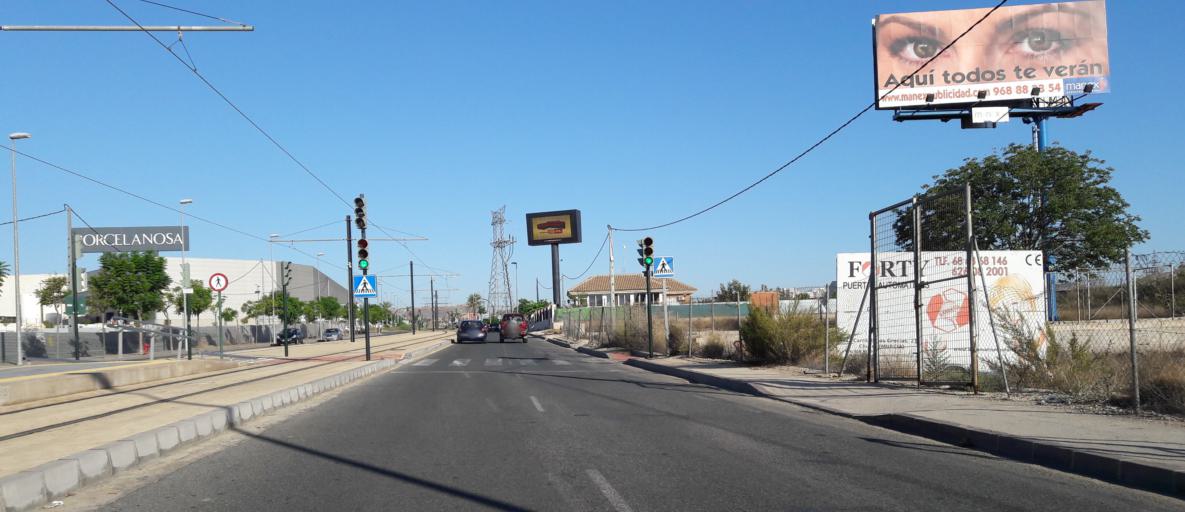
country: ES
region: Murcia
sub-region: Murcia
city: Murcia
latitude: 38.0269
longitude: -1.1423
